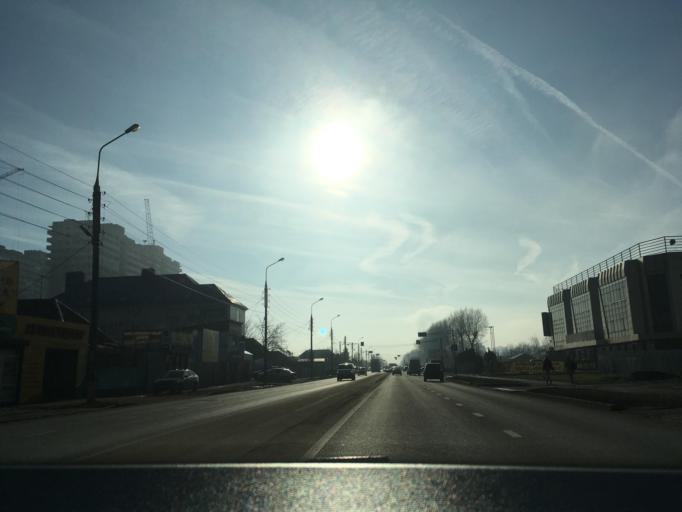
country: RU
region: Krasnodarskiy
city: Krasnodar
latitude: 45.1078
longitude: 39.0125
